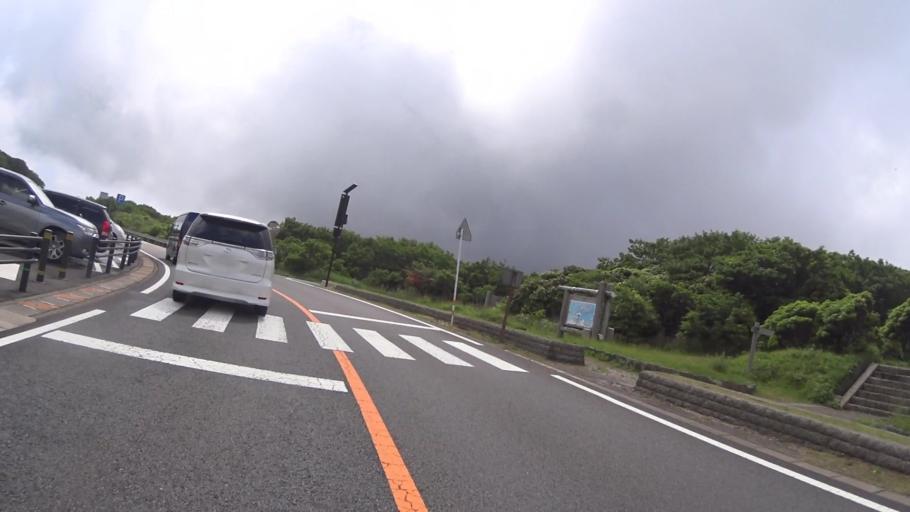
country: JP
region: Oita
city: Tsukawaki
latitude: 33.0965
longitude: 131.2086
